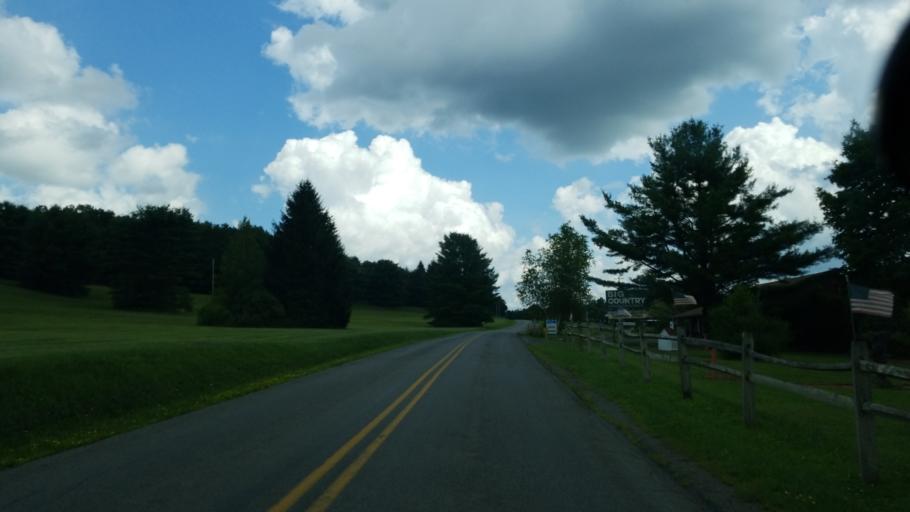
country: US
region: Pennsylvania
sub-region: Jefferson County
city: Brookville
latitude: 41.2322
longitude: -79.0680
